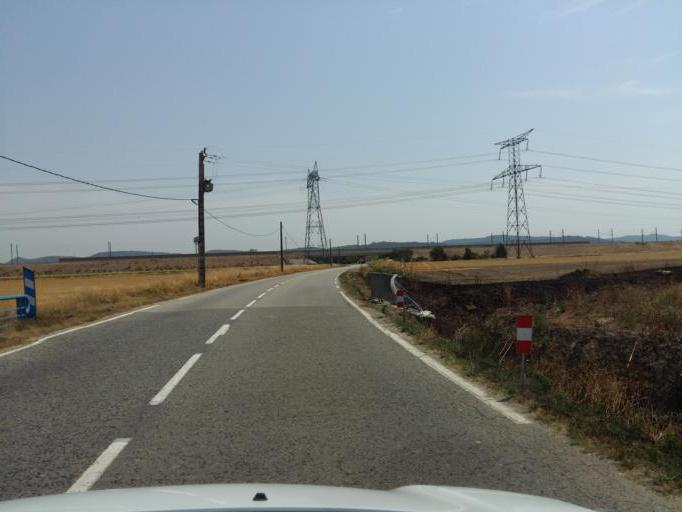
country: FR
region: Provence-Alpes-Cote d'Azur
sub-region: Departement du Vaucluse
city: Mondragon
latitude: 44.2539
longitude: 4.6886
